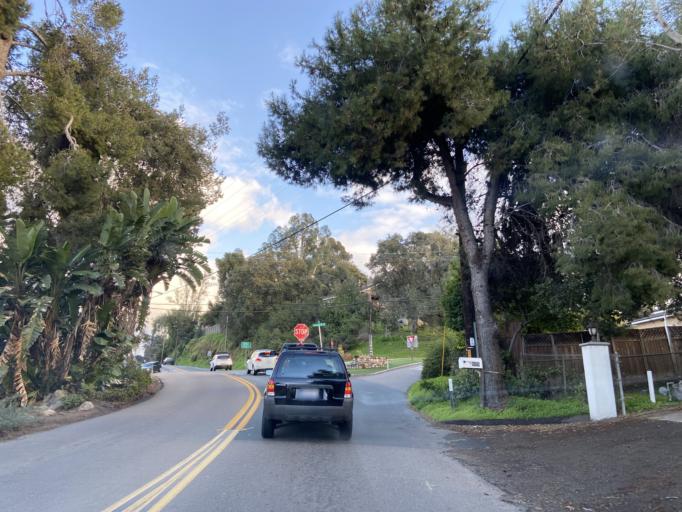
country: US
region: California
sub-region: San Diego County
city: La Mesa
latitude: 32.7780
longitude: -116.9961
